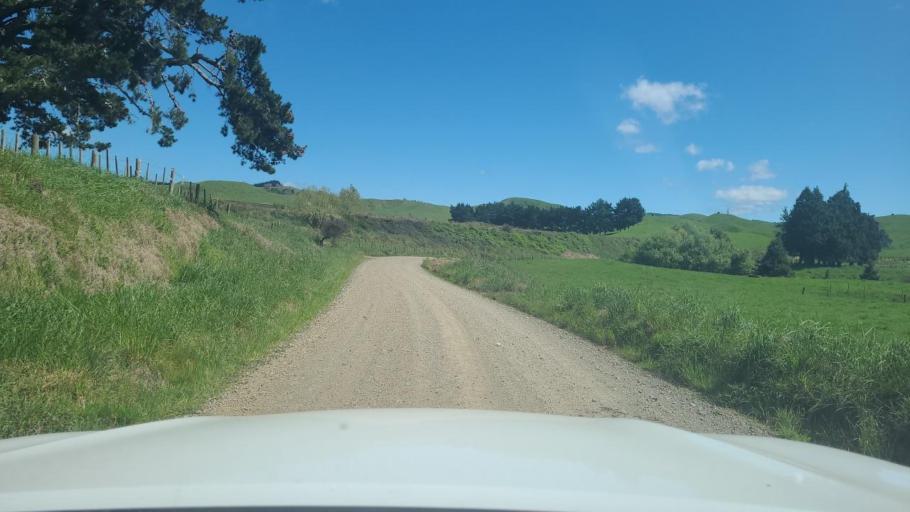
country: NZ
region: Hawke's Bay
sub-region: Napier City
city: Napier
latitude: -39.1388
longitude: 176.9848
